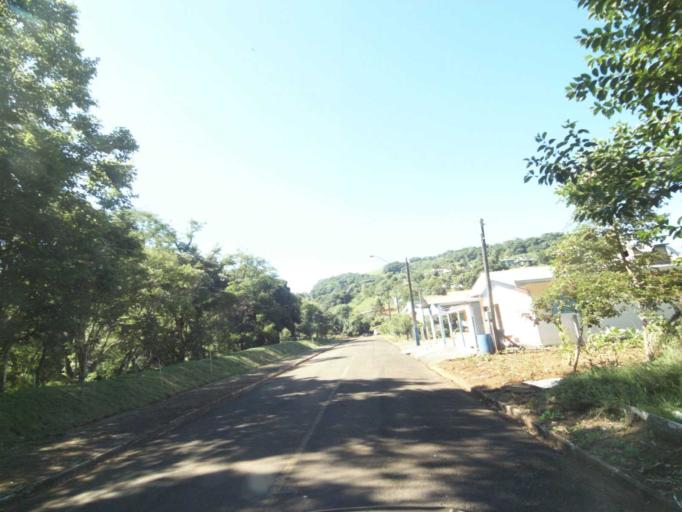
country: BR
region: Parana
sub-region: Francisco Beltrao
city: Francisco Beltrao
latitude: -26.1422
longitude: -53.3086
